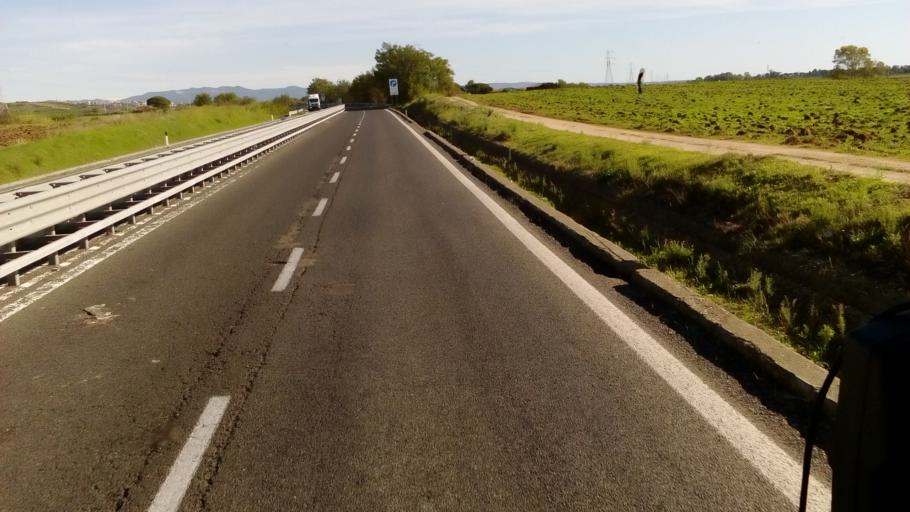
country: IT
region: Latium
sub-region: Provincia di Viterbo
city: Tarquinia
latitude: 42.2839
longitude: 11.6912
